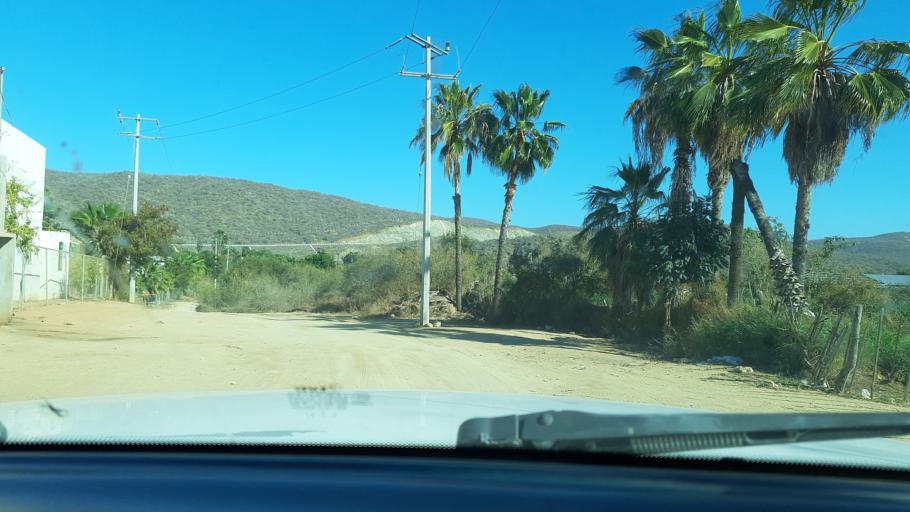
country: MX
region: Baja California Sur
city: Todos Santos
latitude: 23.4738
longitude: -110.2166
